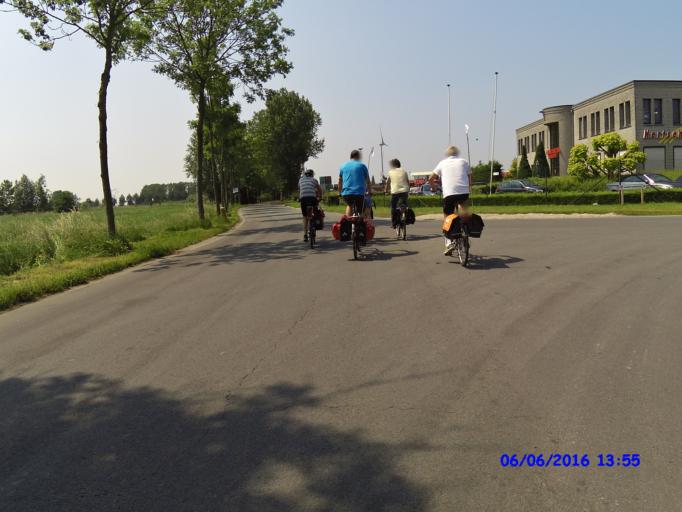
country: BE
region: Flanders
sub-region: Provincie Oost-Vlaanderen
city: Kruibeke
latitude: 51.1932
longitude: 4.3182
